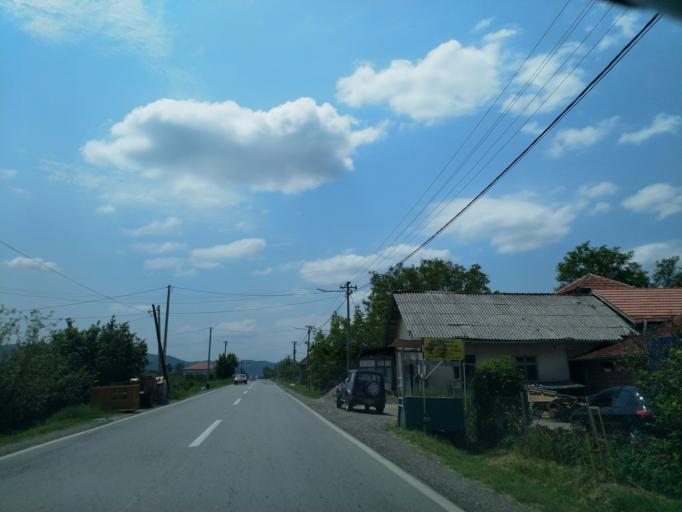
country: RS
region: Central Serbia
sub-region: Rasinski Okrug
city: Krusevac
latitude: 43.4644
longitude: 21.2499
